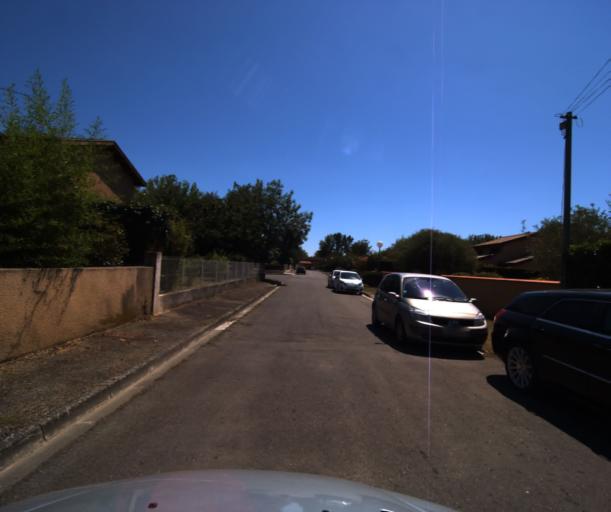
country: FR
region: Midi-Pyrenees
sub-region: Departement de la Haute-Garonne
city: Muret
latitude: 43.4548
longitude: 1.3269
